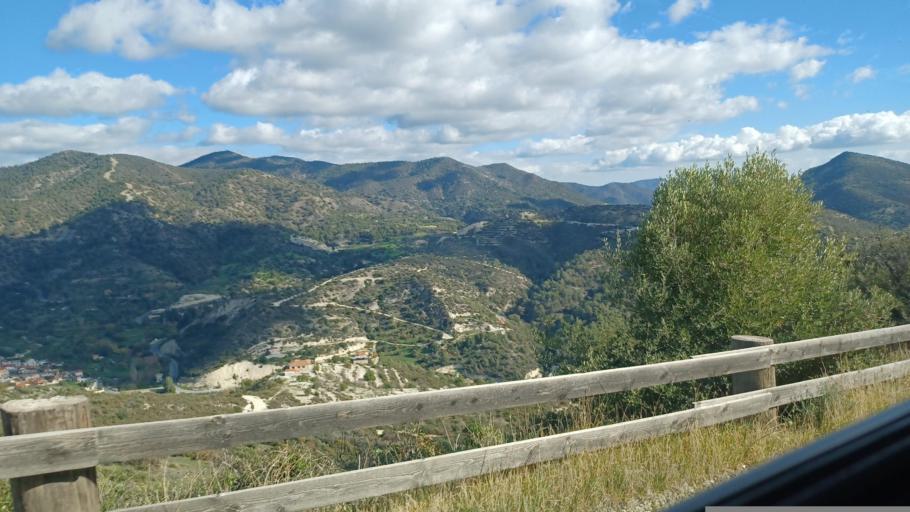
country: CY
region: Limassol
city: Pano Polemidia
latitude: 34.7961
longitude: 32.9911
